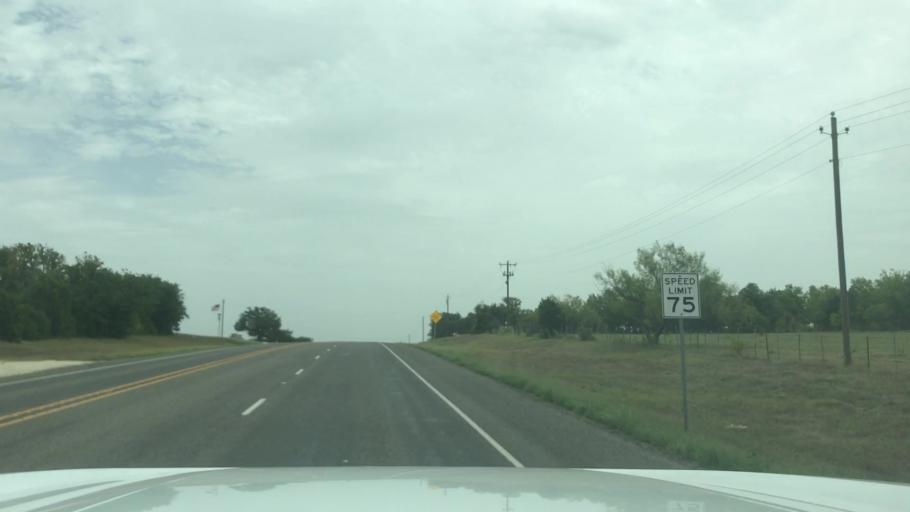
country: US
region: Texas
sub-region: Hamilton County
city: Hico
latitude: 31.9808
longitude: -98.0173
